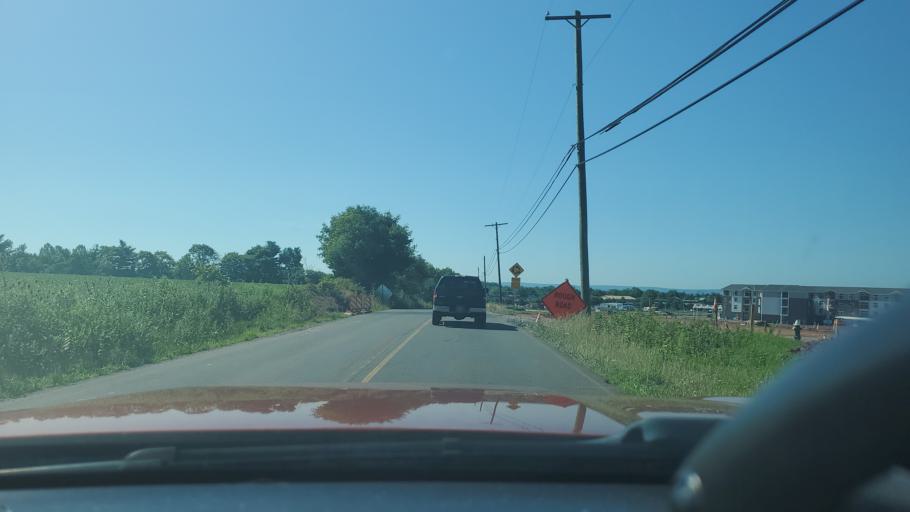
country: US
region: Pennsylvania
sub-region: Montgomery County
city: Limerick
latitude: 40.2378
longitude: -75.5271
